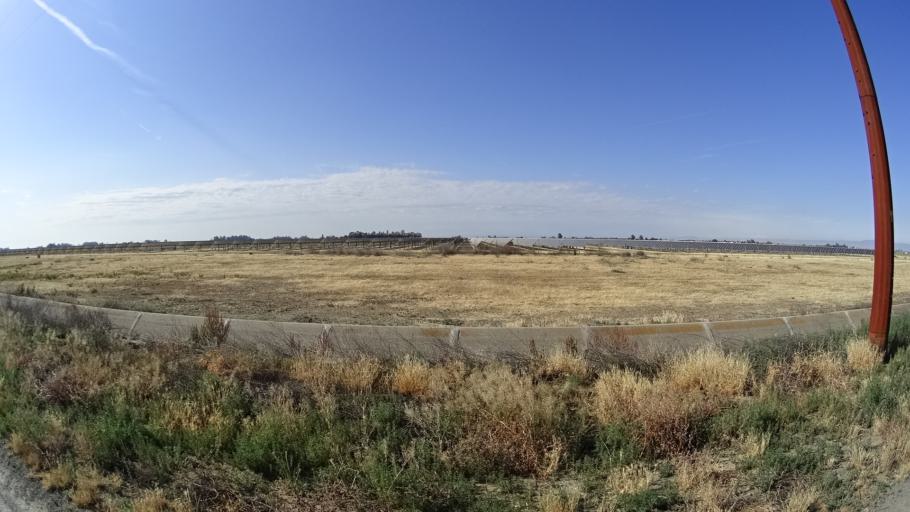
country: US
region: California
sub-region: Kings County
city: Stratford
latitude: 36.2260
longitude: -119.8092
